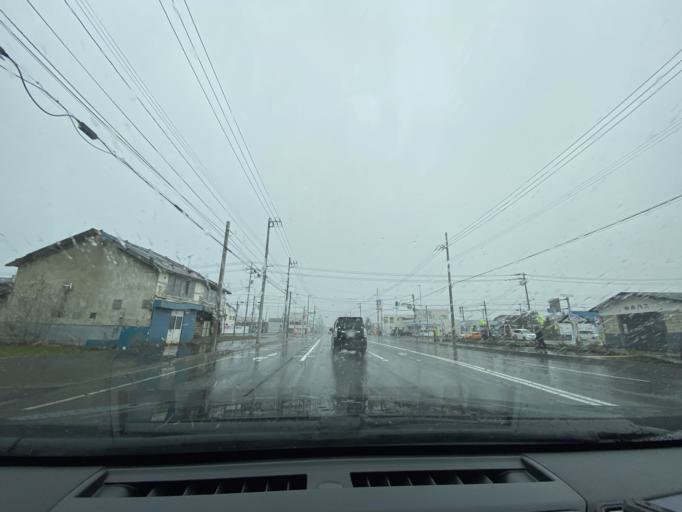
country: JP
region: Hokkaido
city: Takikawa
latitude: 43.6240
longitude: 141.9404
